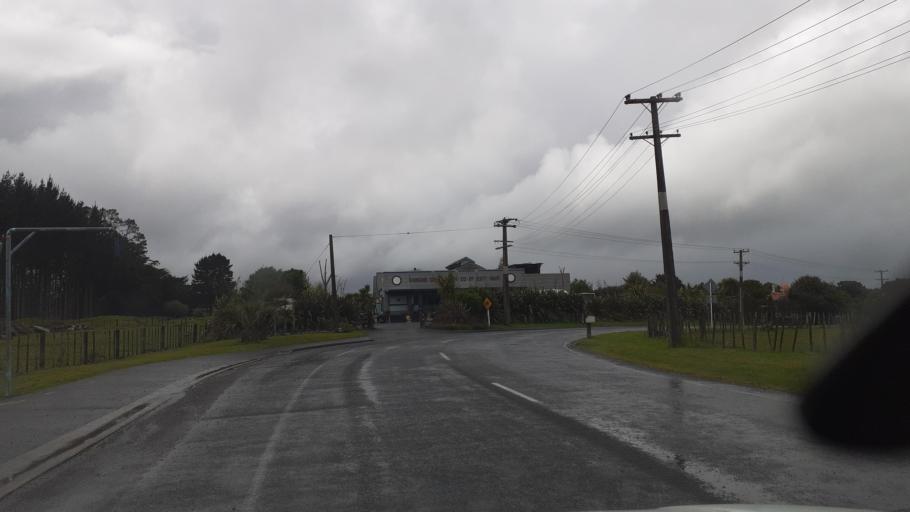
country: NZ
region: Northland
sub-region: Far North District
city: Waimate North
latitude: -35.4147
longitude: 173.7998
